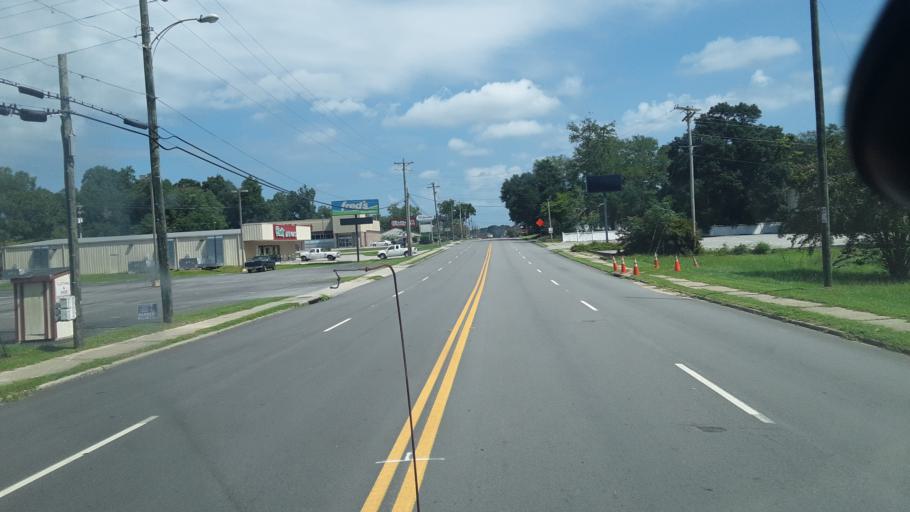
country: US
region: South Carolina
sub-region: Bamberg County
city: Bamberg
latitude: 33.2889
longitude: -81.0381
